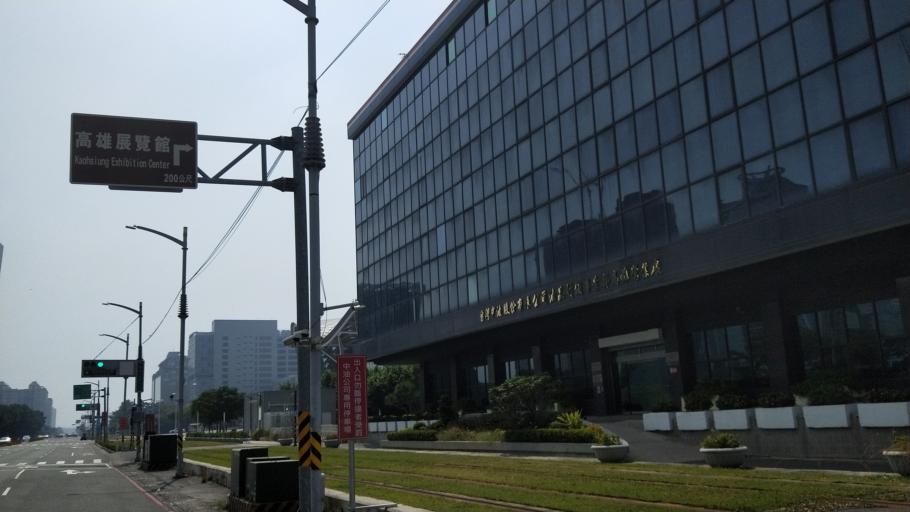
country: TW
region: Kaohsiung
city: Kaohsiung
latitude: 22.6099
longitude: 120.2993
